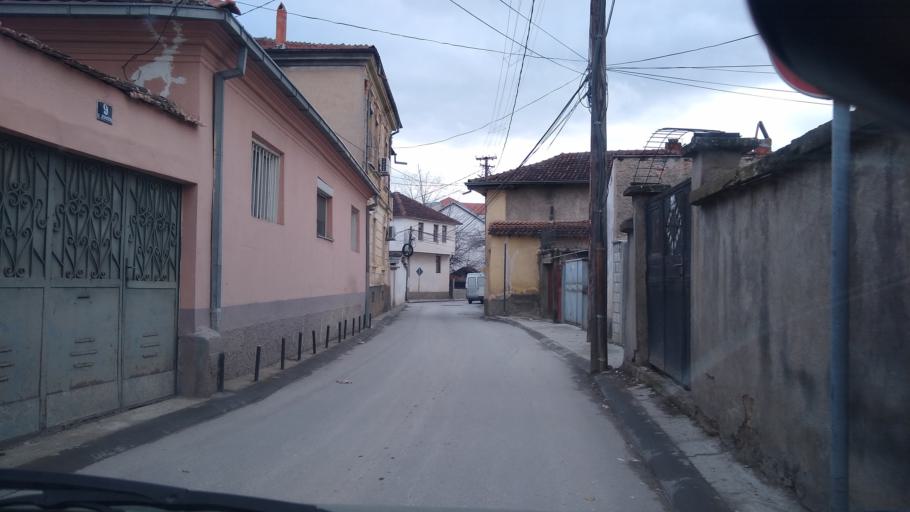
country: MK
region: Bitola
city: Bitola
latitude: 41.0284
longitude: 21.3305
